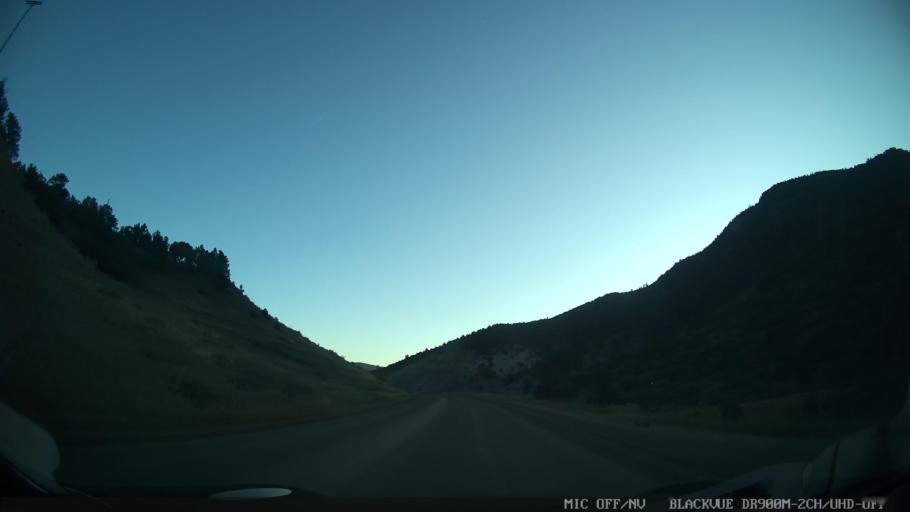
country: US
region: Colorado
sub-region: Eagle County
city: Edwards
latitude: 39.8730
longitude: -106.6364
